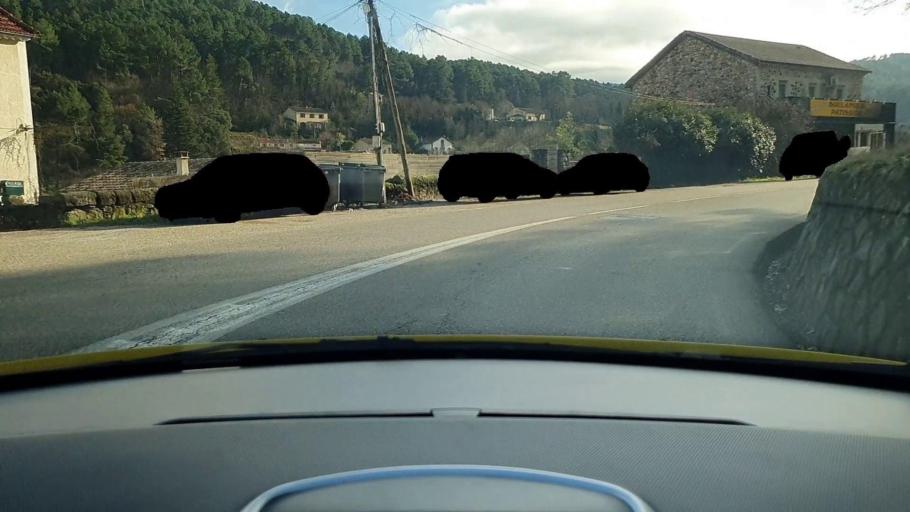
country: FR
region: Languedoc-Roussillon
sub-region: Departement du Gard
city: Branoux-les-Taillades
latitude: 44.3033
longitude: 3.9774
